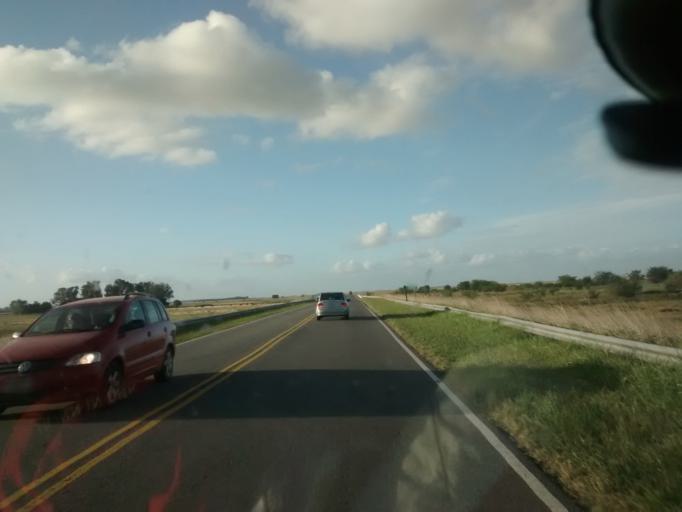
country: AR
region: Buenos Aires
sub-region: Partido de General Belgrano
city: General Belgrano
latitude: -36.1334
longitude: -58.5935
